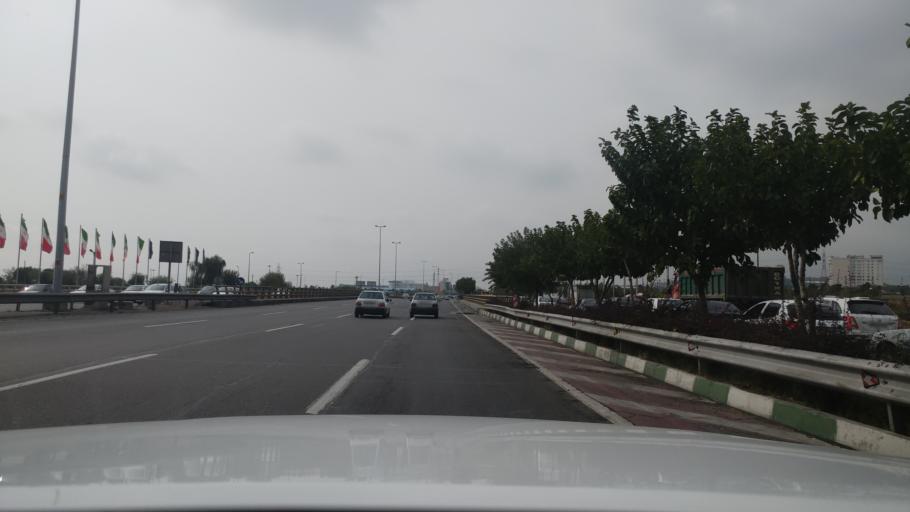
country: IR
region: Tehran
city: Shahr-e Qods
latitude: 35.7146
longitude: 51.2533
